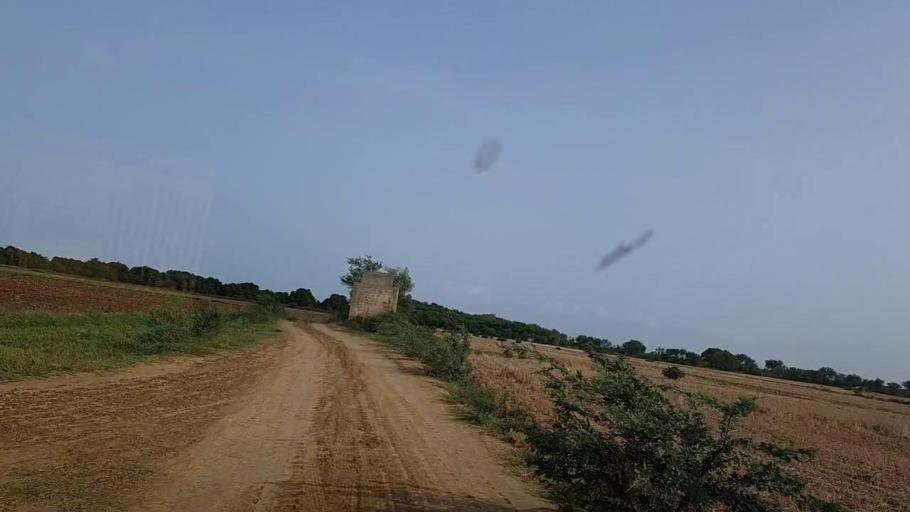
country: PK
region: Sindh
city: Kotri
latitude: 25.2391
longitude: 68.2448
